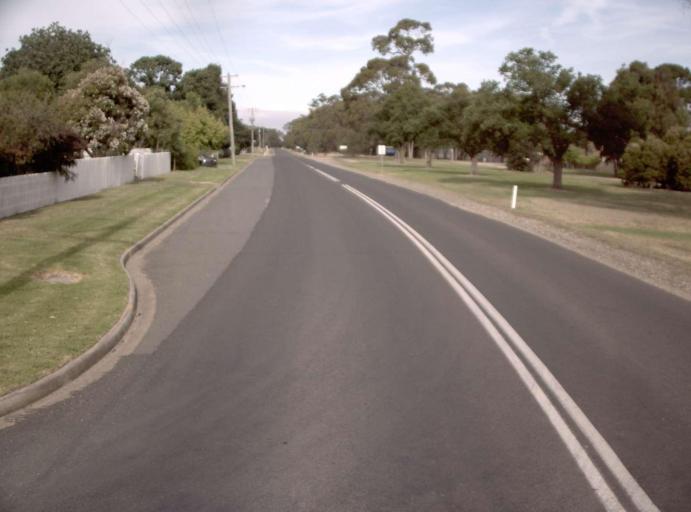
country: AU
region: Victoria
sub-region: Latrobe
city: Traralgon
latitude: -38.0601
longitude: 146.6281
